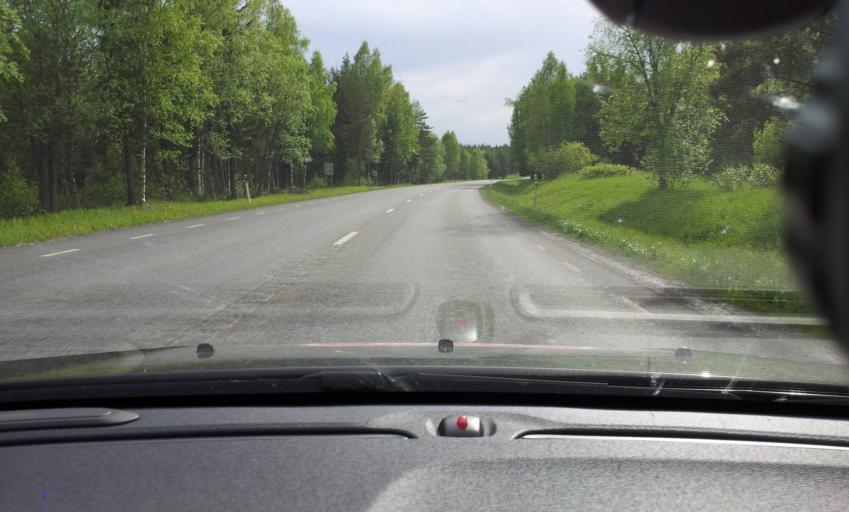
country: SE
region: Jaemtland
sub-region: OEstersunds Kommun
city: Ostersund
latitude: 63.1840
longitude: 14.7255
